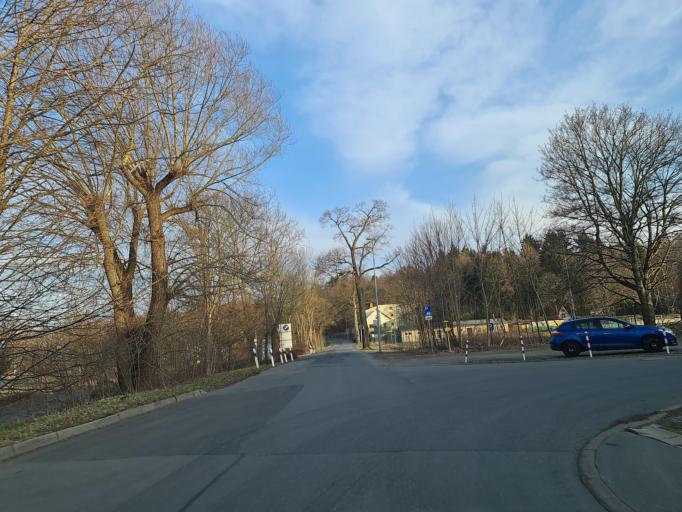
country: DE
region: Saxony
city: Plauen
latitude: 50.5203
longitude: 12.1141
